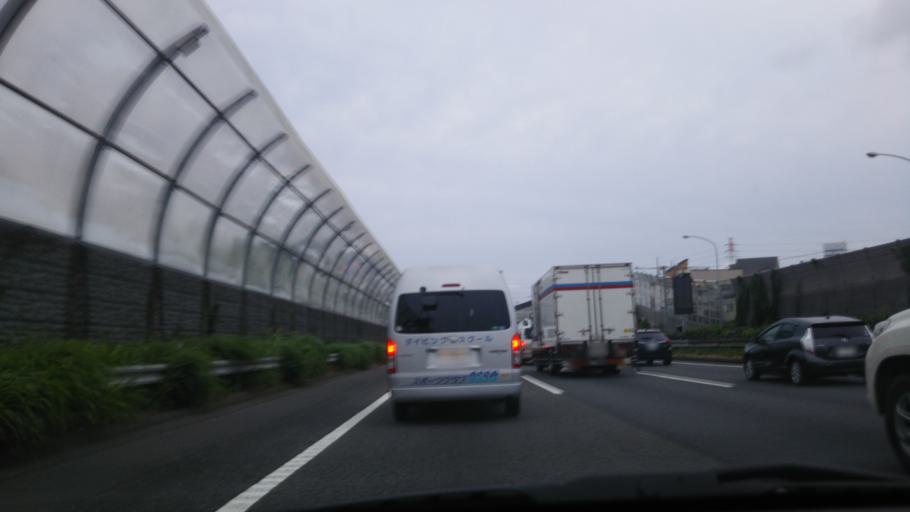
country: JP
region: Kanagawa
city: Minami-rinkan
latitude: 35.4537
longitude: 139.4264
